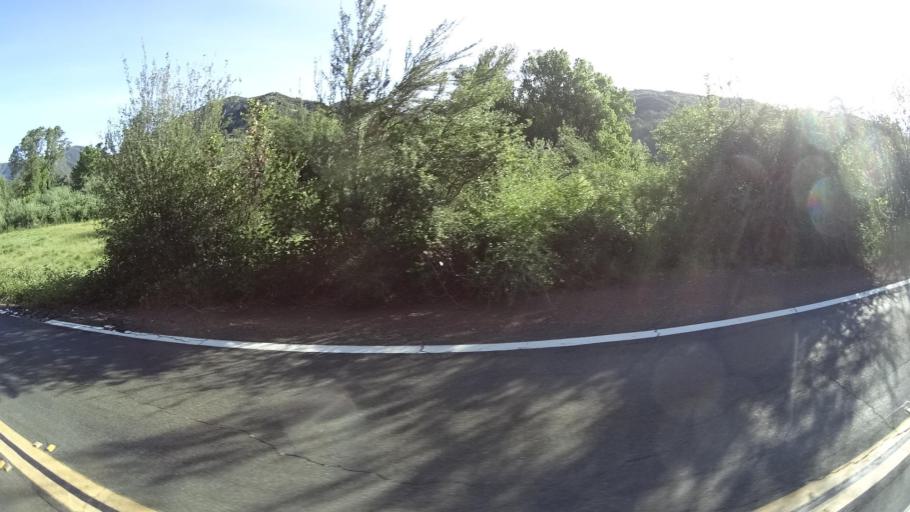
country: US
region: California
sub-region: Lake County
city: Upper Lake
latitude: 39.1217
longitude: -122.9901
